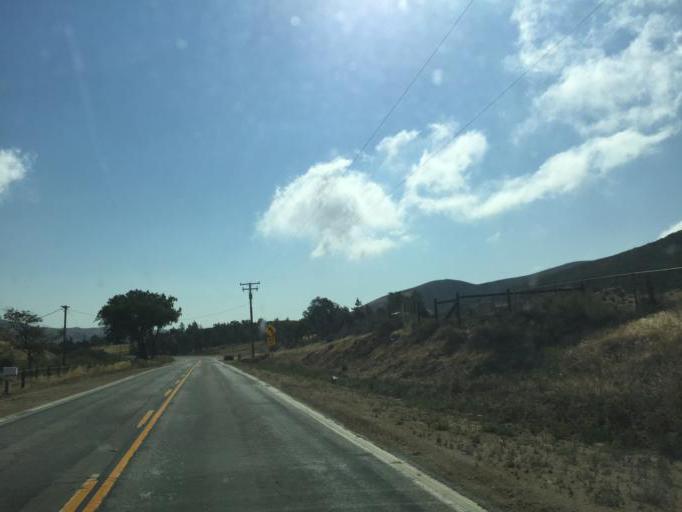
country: US
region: California
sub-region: Los Angeles County
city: Leona Valley
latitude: 34.5912
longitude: -118.2809
